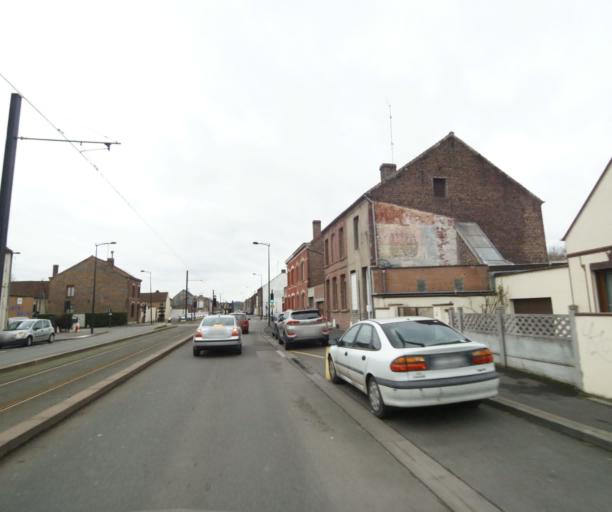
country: FR
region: Nord-Pas-de-Calais
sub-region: Departement du Nord
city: Bruay-sur-l'Escaut
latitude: 50.4023
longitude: 3.5459
